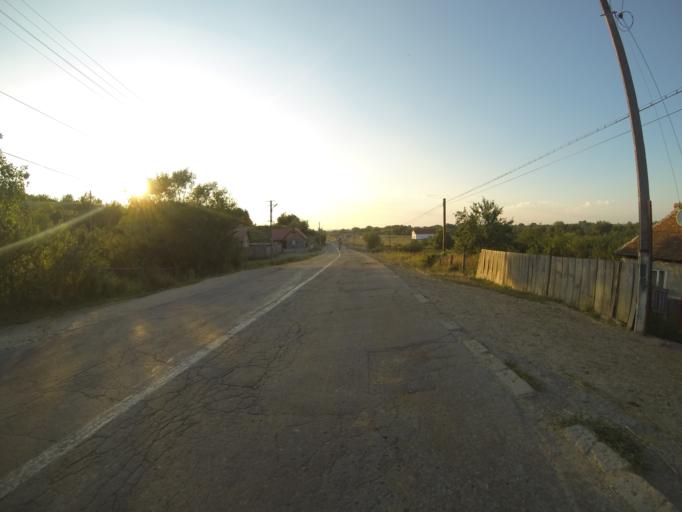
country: RO
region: Brasov
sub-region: Comuna Sinca Veche
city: Sinca Veche
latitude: 45.7557
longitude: 25.1760
